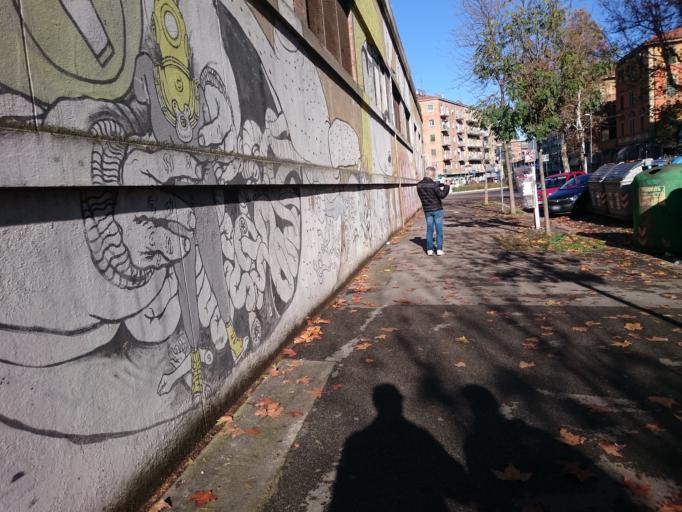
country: IT
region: Emilia-Romagna
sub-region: Provincia di Bologna
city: Bologna
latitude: 44.5122
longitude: 11.3414
